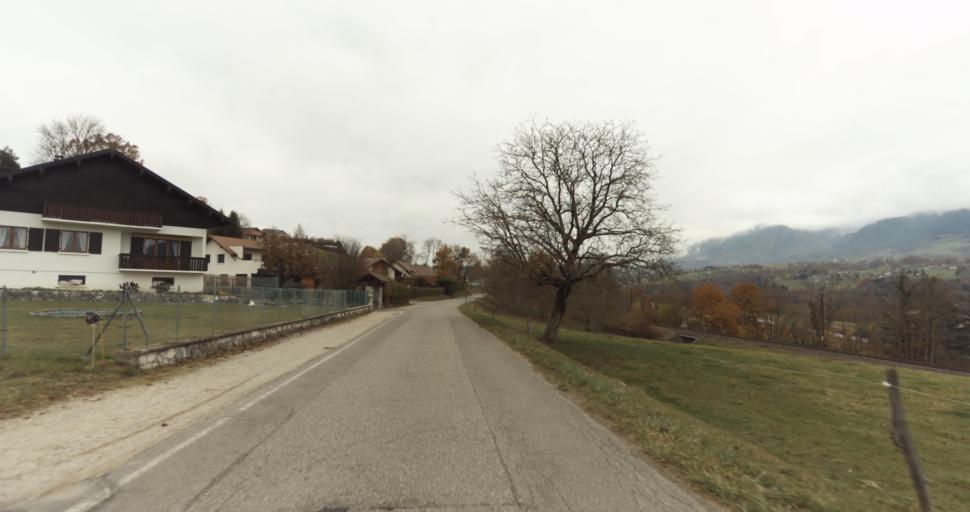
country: FR
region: Rhone-Alpes
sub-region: Departement de la Haute-Savoie
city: Saint-Martin-Bellevue
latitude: 45.9467
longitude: 6.1536
